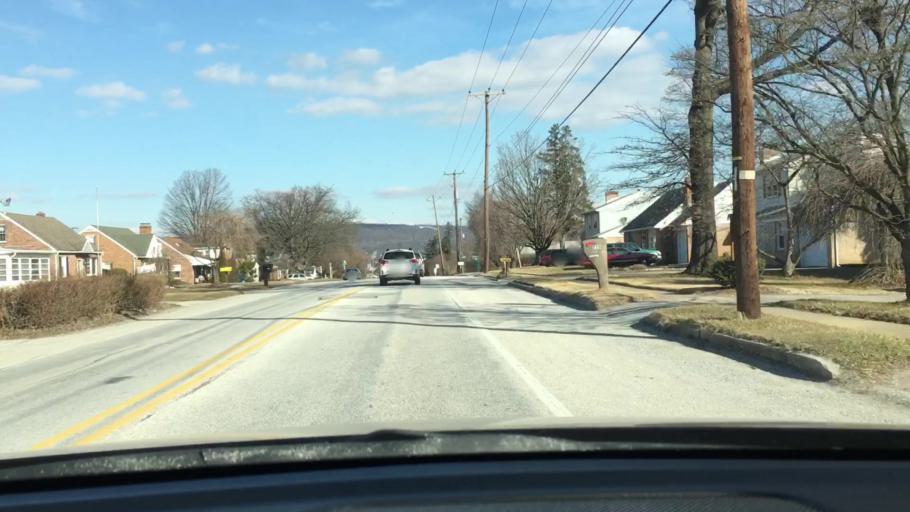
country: US
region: Pennsylvania
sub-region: York County
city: Stonybrook
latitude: 39.9735
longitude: -76.6600
